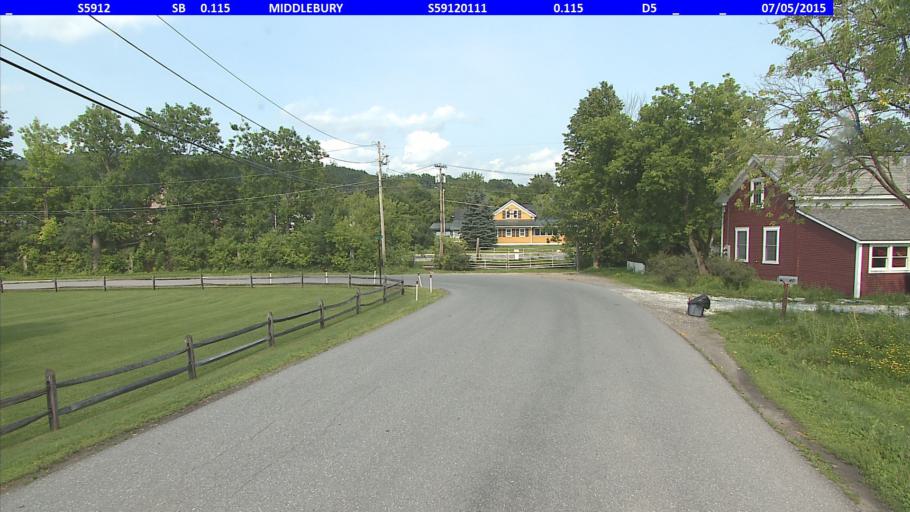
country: US
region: Vermont
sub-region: Addison County
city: Middlebury (village)
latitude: 44.0170
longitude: -73.1702
